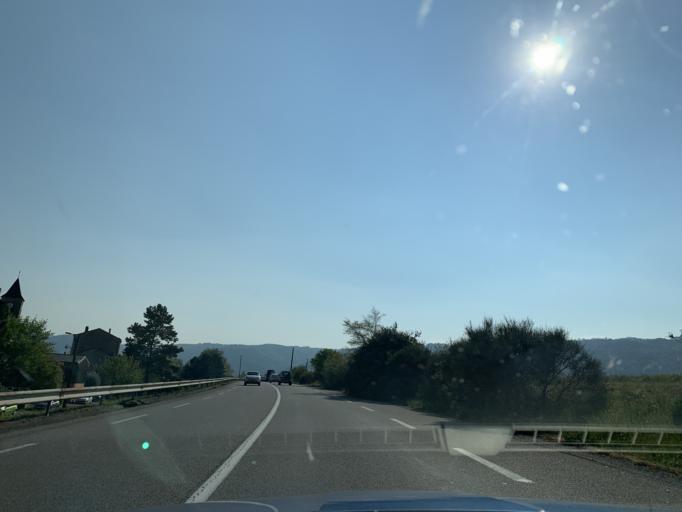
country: FR
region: Rhone-Alpes
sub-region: Departement de la Drome
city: Saint-Vallier
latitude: 45.1412
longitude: 4.8187
